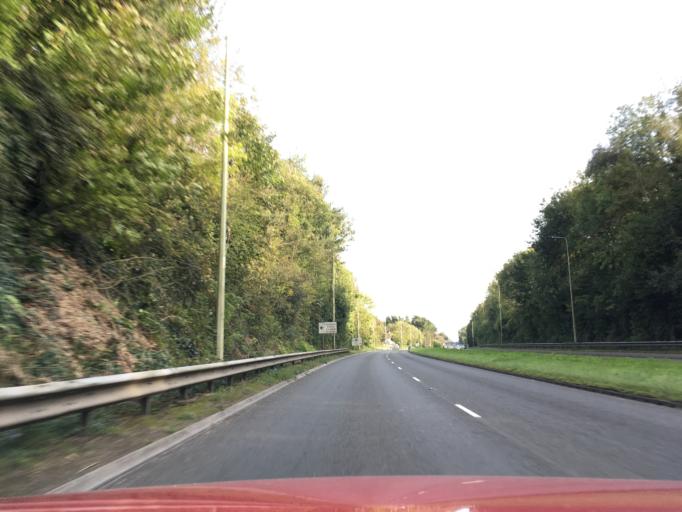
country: GB
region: Wales
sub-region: Rhondda Cynon Taf
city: Llantrisant
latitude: 51.5294
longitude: -3.3681
